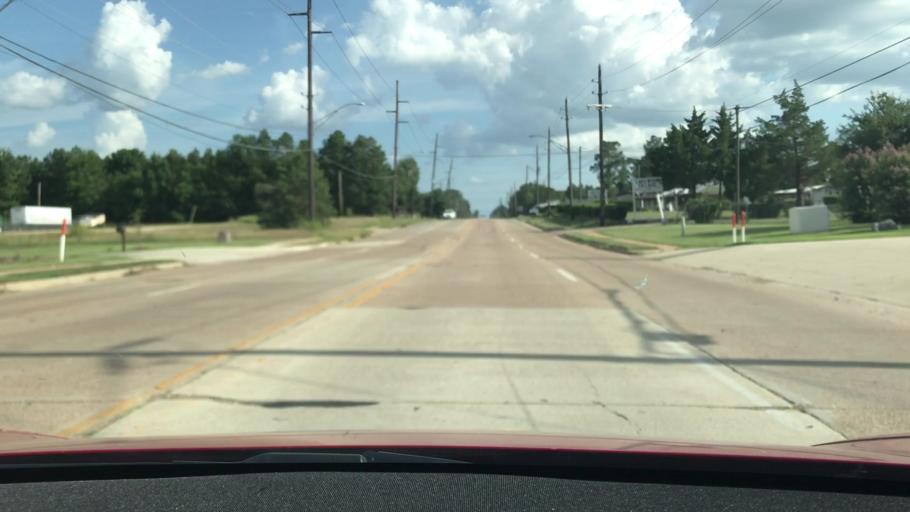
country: US
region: Louisiana
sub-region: Bossier Parish
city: Bossier City
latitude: 32.4181
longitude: -93.7632
